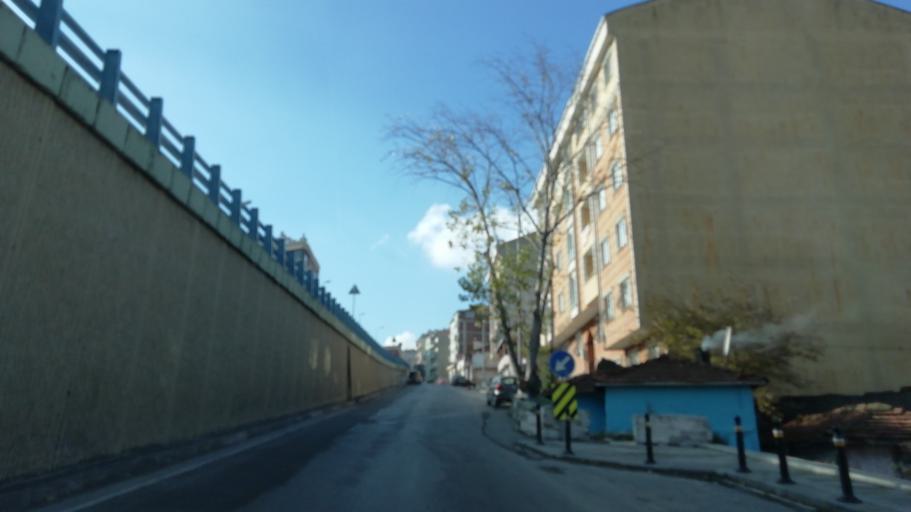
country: TR
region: Istanbul
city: Istanbul
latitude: 41.0606
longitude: 28.9335
